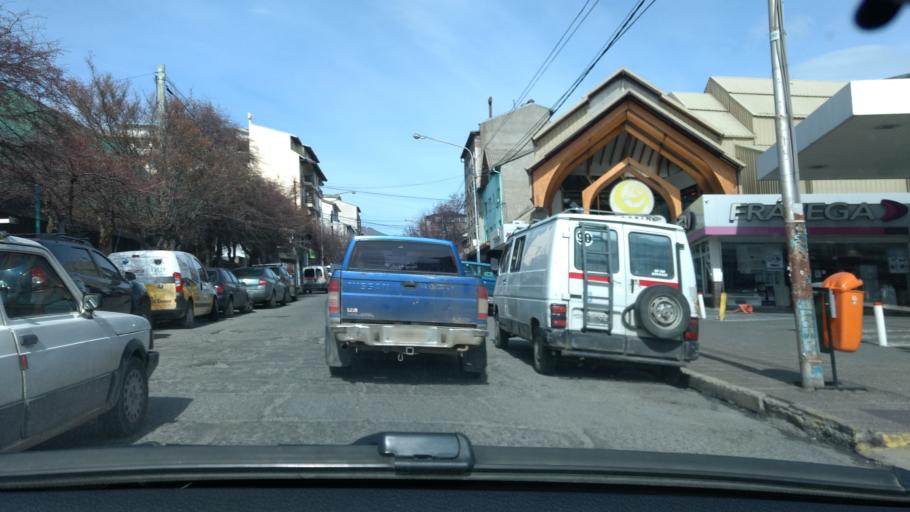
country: AR
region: Rio Negro
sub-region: Departamento de Bariloche
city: San Carlos de Bariloche
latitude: -41.1370
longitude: -71.2974
